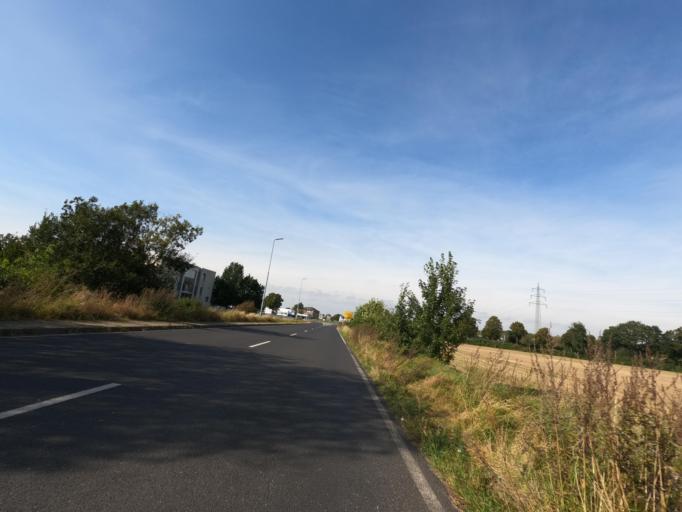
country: DE
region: North Rhine-Westphalia
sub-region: Regierungsbezirk Koln
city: Linnich
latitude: 50.9796
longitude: 6.2866
